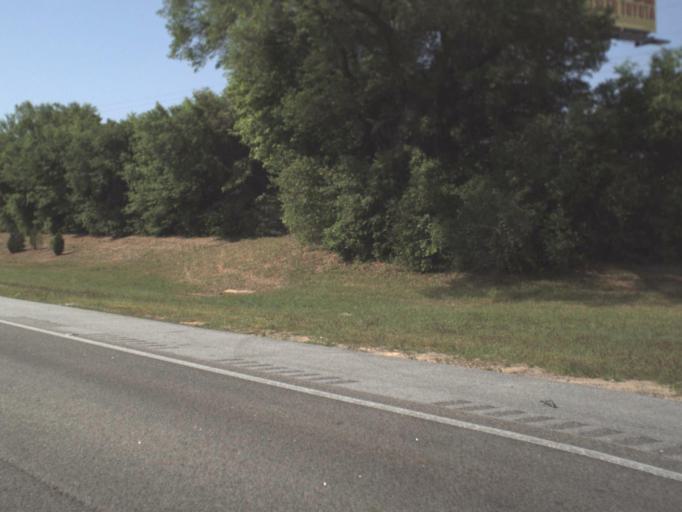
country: US
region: Florida
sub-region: Escambia County
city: Goulding
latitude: 30.4574
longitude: -87.2245
